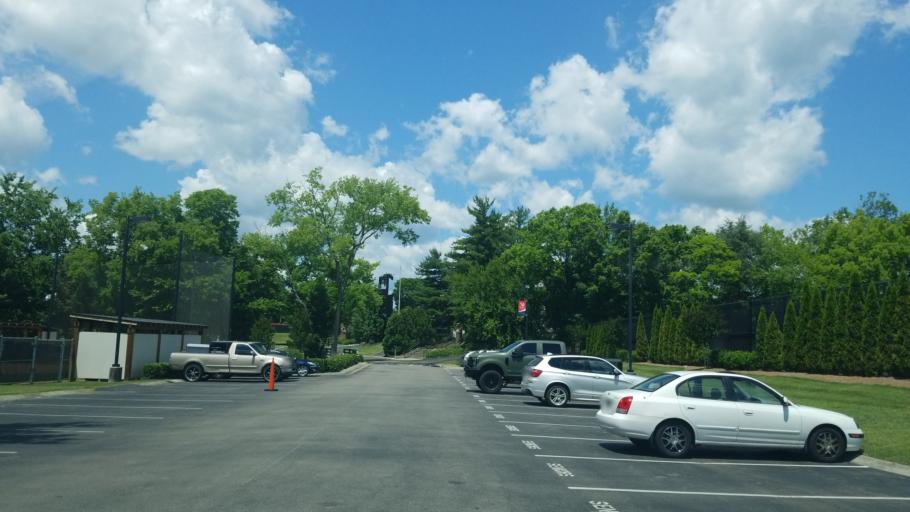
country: US
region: Tennessee
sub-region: Williamson County
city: Brentwood
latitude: 36.0324
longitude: -86.8193
